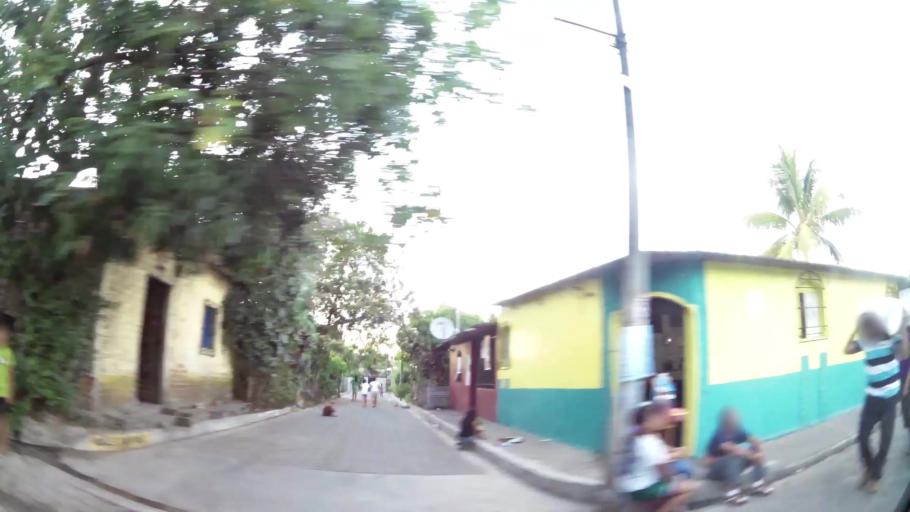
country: SV
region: La Libertad
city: Santa Tecla
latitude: 13.7332
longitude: -89.3787
